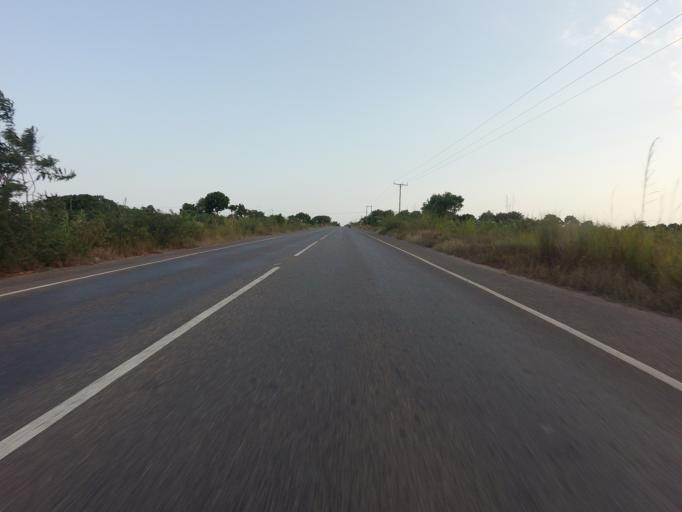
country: GH
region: Volta
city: Anloga
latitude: 6.0665
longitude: 0.6045
